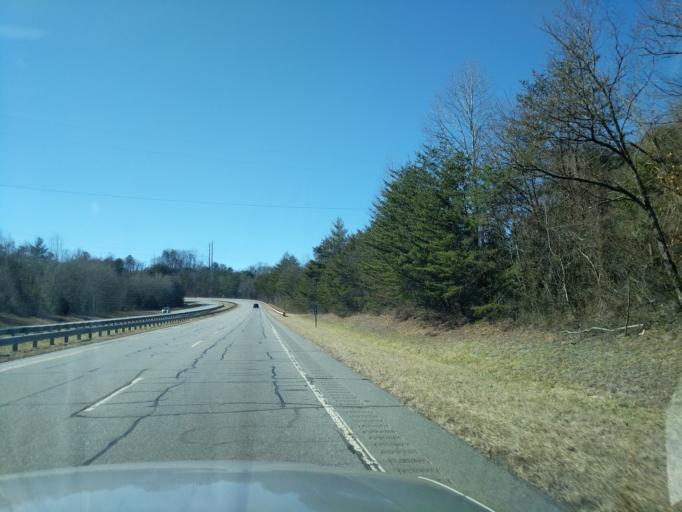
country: US
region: North Carolina
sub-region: Swain County
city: Bryson City
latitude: 35.4133
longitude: -83.4496
